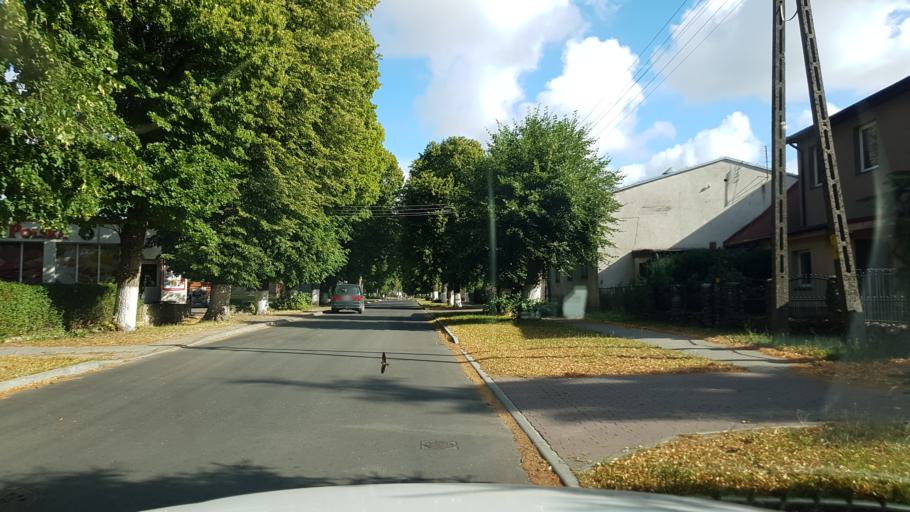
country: PL
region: West Pomeranian Voivodeship
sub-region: Powiat mysliborski
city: Debno
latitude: 52.7372
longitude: 14.6663
